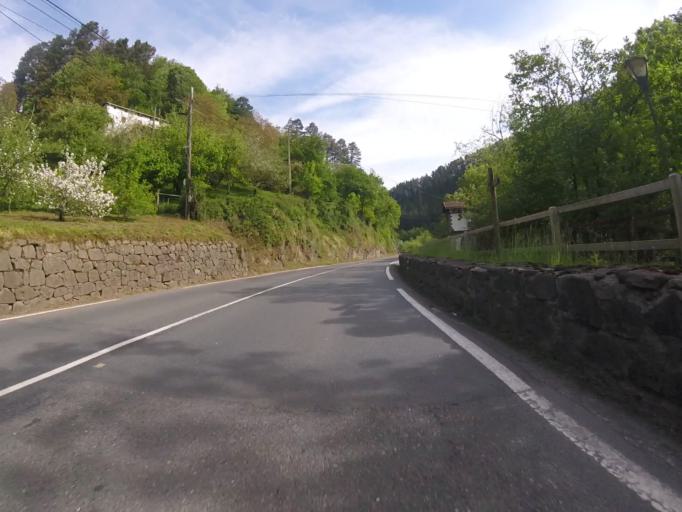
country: ES
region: Basque Country
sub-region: Provincia de Guipuzcoa
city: Urretxu
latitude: 43.1019
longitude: -2.3177
